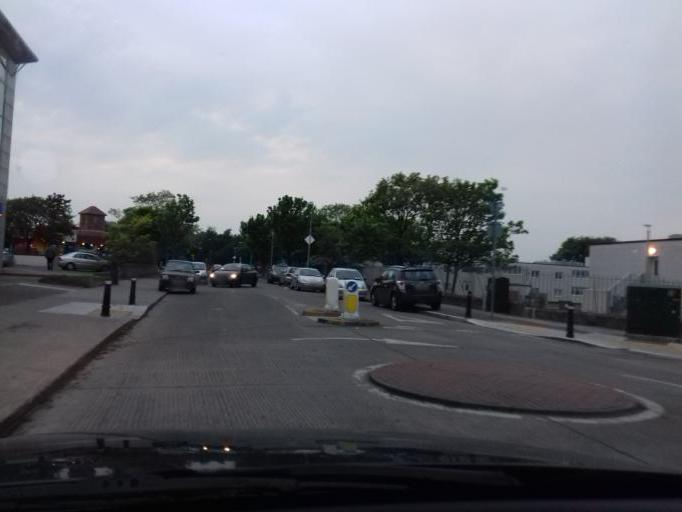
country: IE
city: Bayside
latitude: 53.3853
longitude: -6.1536
